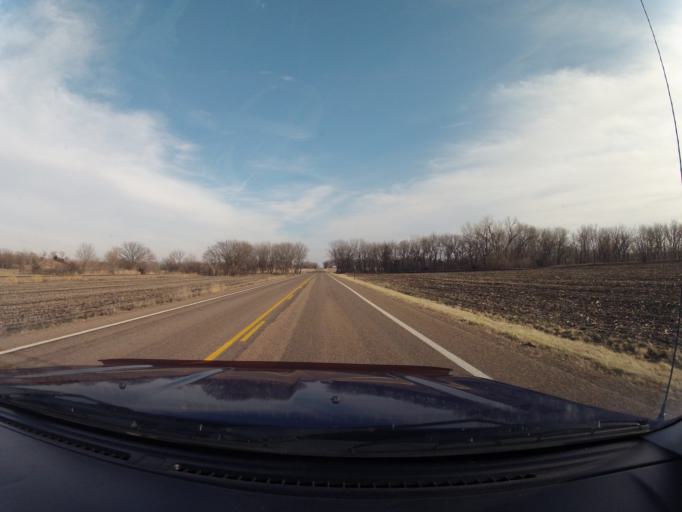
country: US
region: Kansas
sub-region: Pottawatomie County
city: Saint Marys
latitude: 39.2159
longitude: -96.1206
